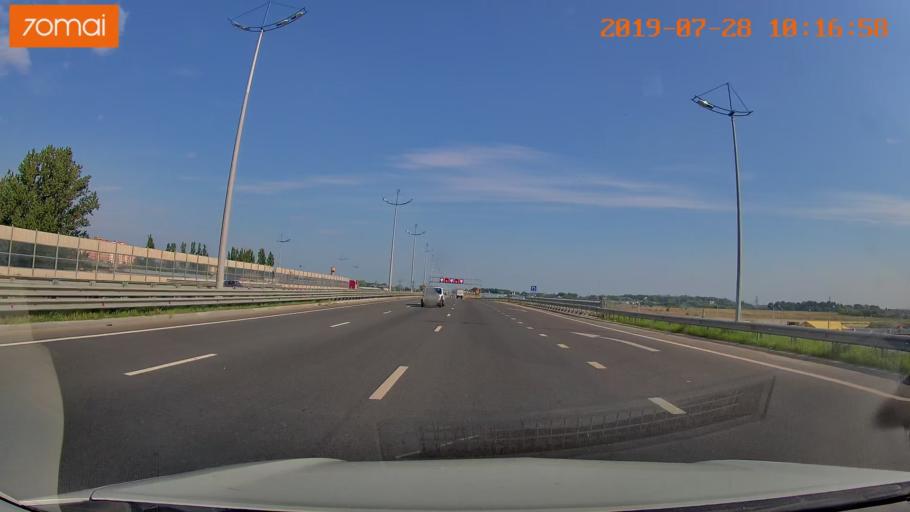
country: RU
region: Kaliningrad
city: Maloye Isakovo
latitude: 54.7337
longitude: 20.5973
